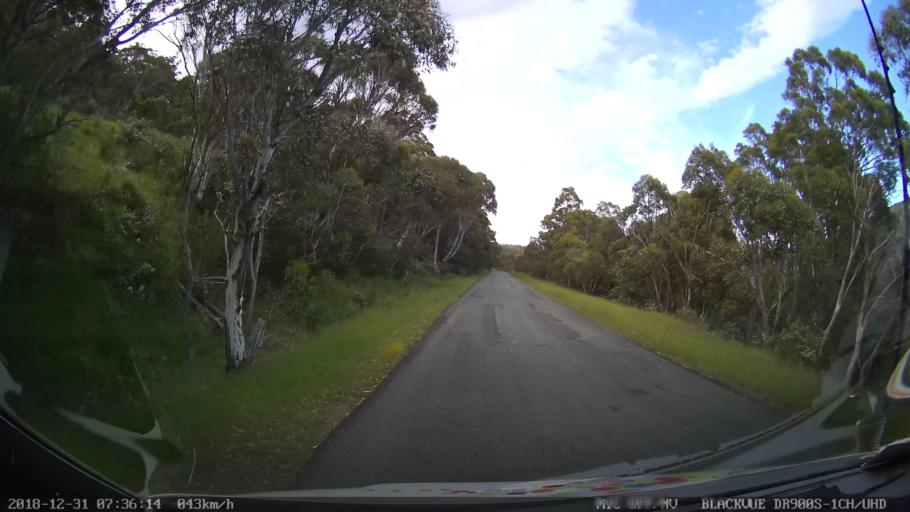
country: AU
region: New South Wales
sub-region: Snowy River
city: Jindabyne
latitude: -36.3397
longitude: 148.4436
